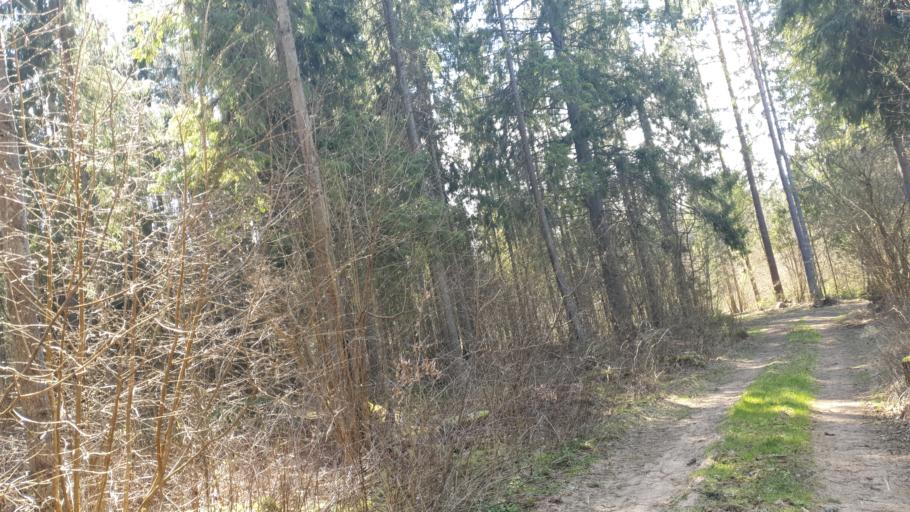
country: LT
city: Aukstadvaris
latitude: 54.4931
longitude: 24.6517
